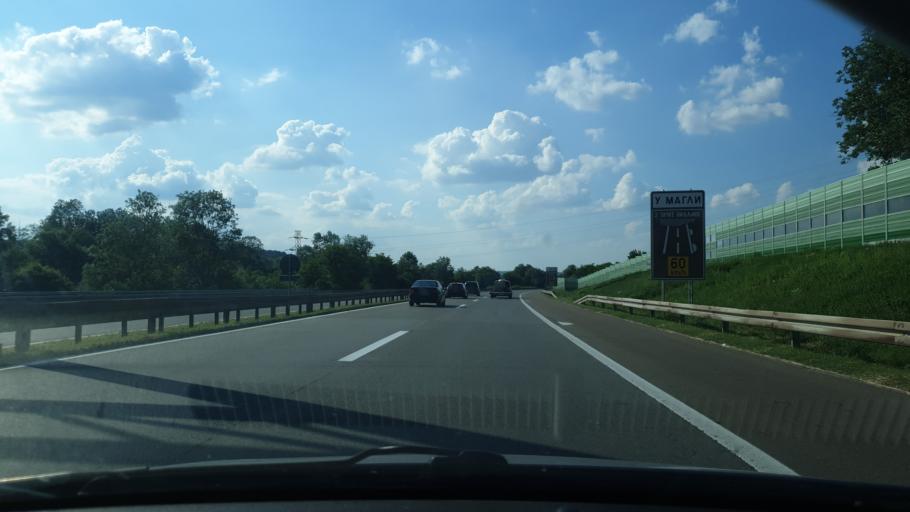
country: RS
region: Central Serbia
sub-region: Belgrade
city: Zvezdara
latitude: 44.6769
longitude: 20.5891
